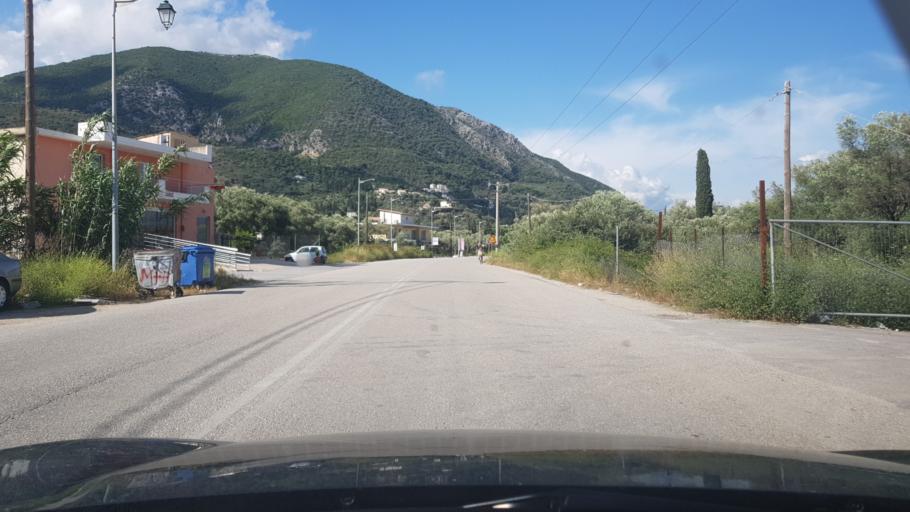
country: GR
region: Ionian Islands
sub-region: Lefkada
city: Nidri
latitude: 38.7086
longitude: 20.7047
